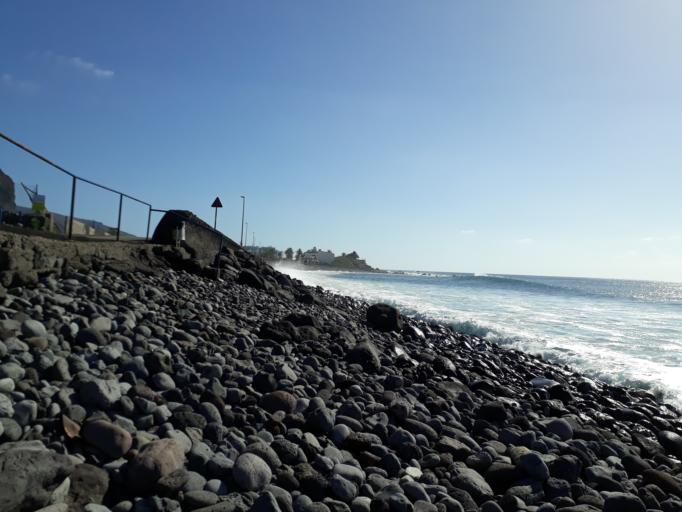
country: ES
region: Canary Islands
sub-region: Provincia de Santa Cruz de Tenerife
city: Alajero
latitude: 28.0917
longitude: -17.3402
